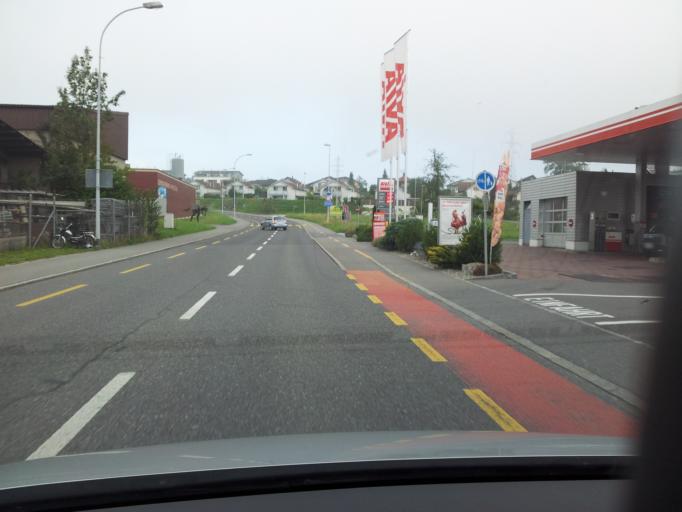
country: CH
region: Lucerne
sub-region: Hochdorf District
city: Emmen
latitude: 47.1006
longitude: 8.2675
